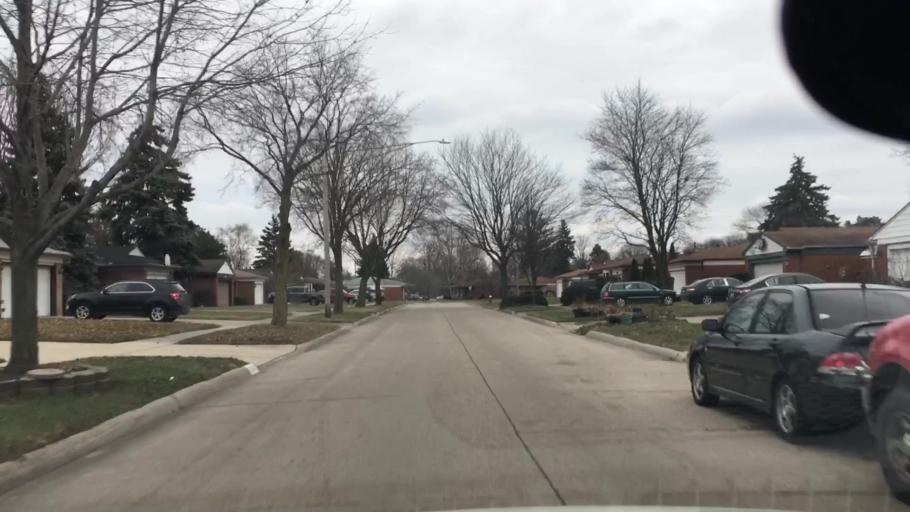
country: US
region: Michigan
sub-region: Oakland County
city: Madison Heights
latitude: 42.4968
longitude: -83.0711
